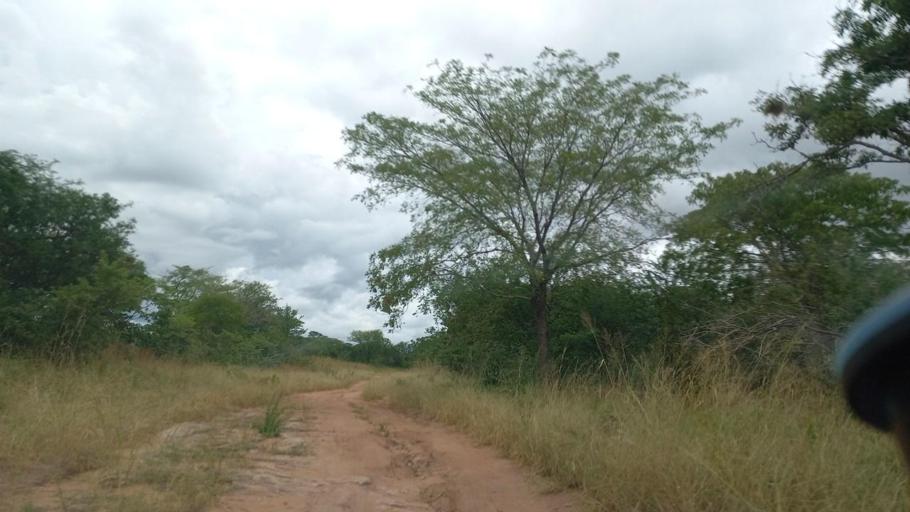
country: ZM
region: Lusaka
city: Luangwa
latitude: -15.5687
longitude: 30.3214
